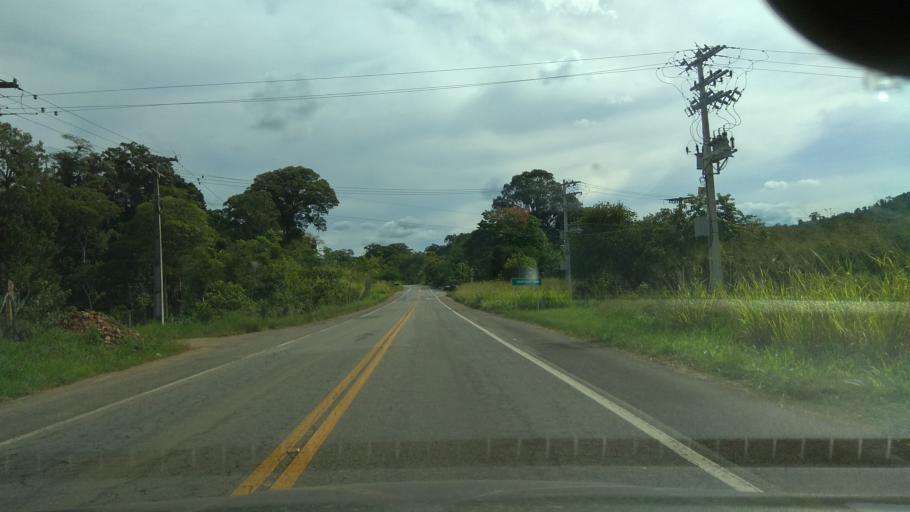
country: BR
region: Bahia
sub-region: Ubata
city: Ubata
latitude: -14.2290
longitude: -39.4452
